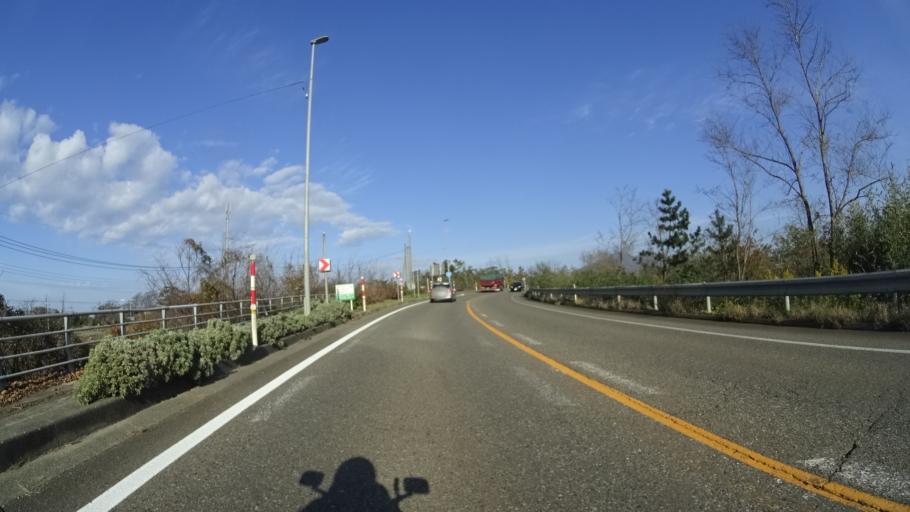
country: JP
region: Niigata
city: Joetsu
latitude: 37.2626
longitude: 138.3728
